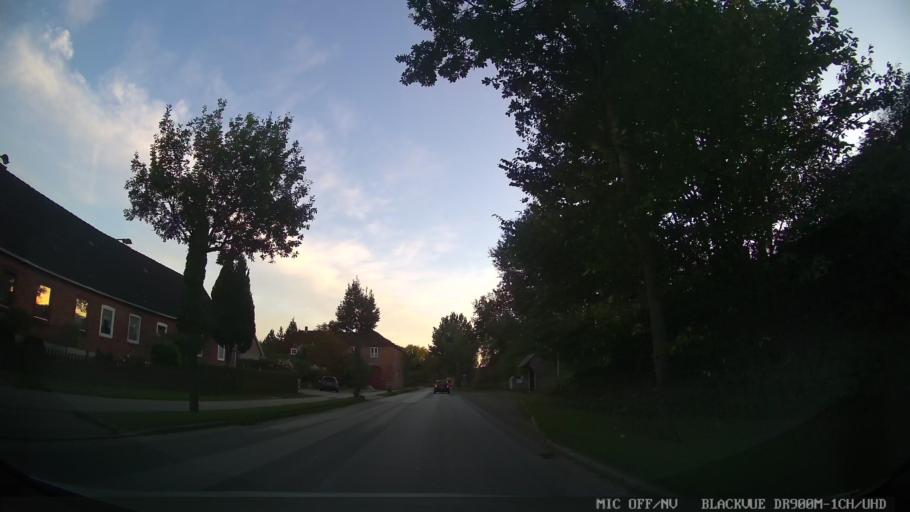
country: DE
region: Schleswig-Holstein
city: Susel
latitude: 54.0598
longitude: 10.6851
